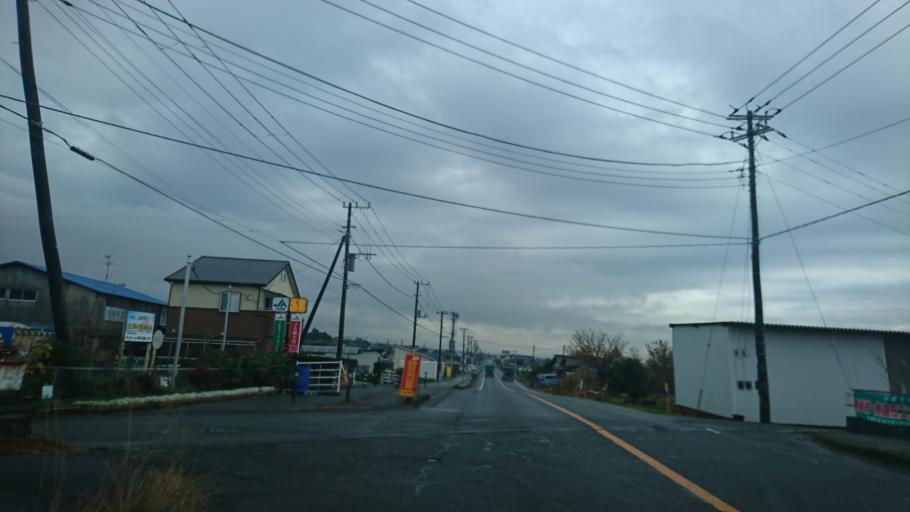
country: JP
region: Shizuoka
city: Fuji
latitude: 35.1503
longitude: 138.7648
